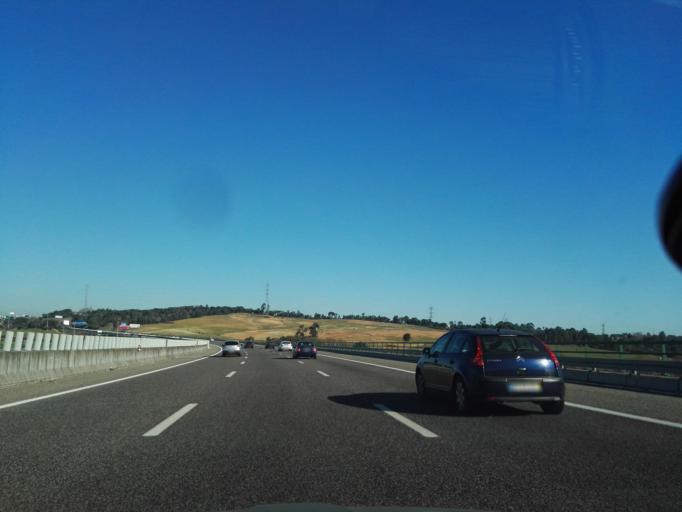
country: PT
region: Santarem
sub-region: Santarem
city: Santarem
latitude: 39.2419
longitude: -8.7460
